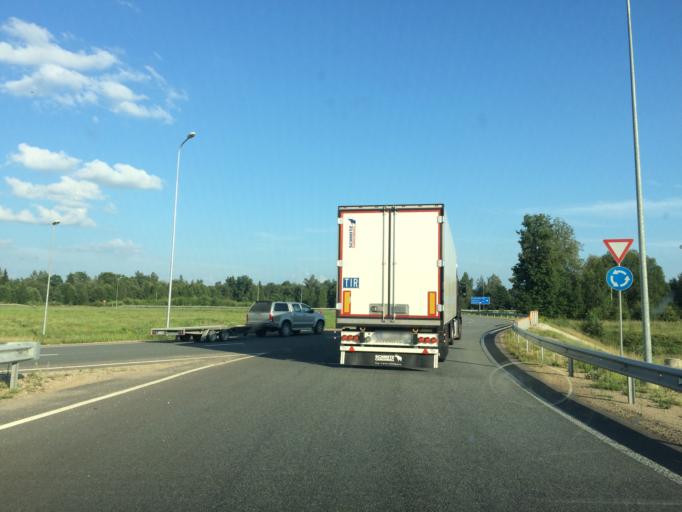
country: LV
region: Koknese
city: Koknese
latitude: 56.6658
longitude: 25.4642
